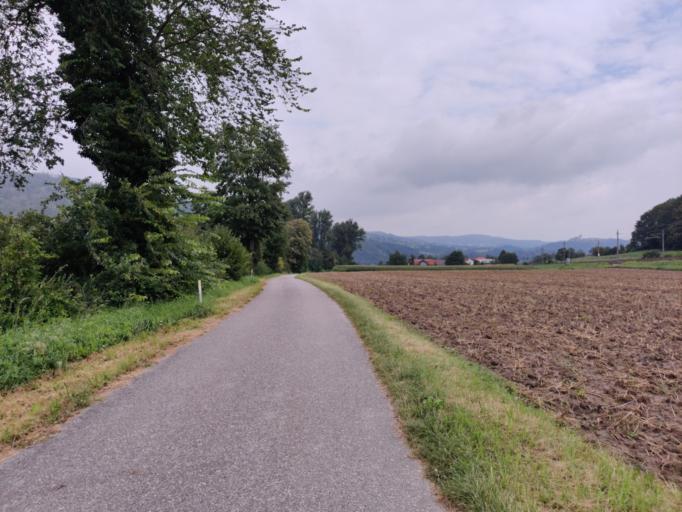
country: AT
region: Lower Austria
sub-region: Politischer Bezirk Melk
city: Marbach an der Donau
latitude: 48.1979
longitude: 15.1129
